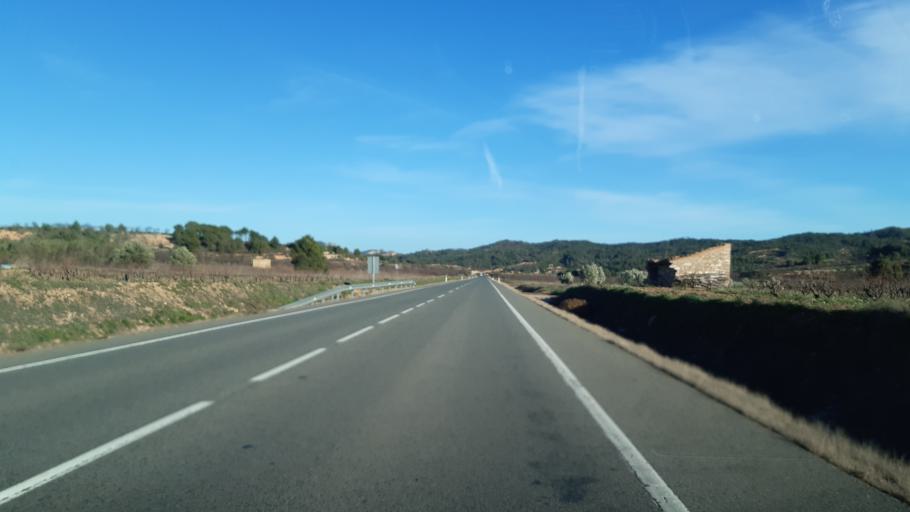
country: ES
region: Catalonia
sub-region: Provincia de Tarragona
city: Gandesa
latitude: 41.0847
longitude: 0.4946
